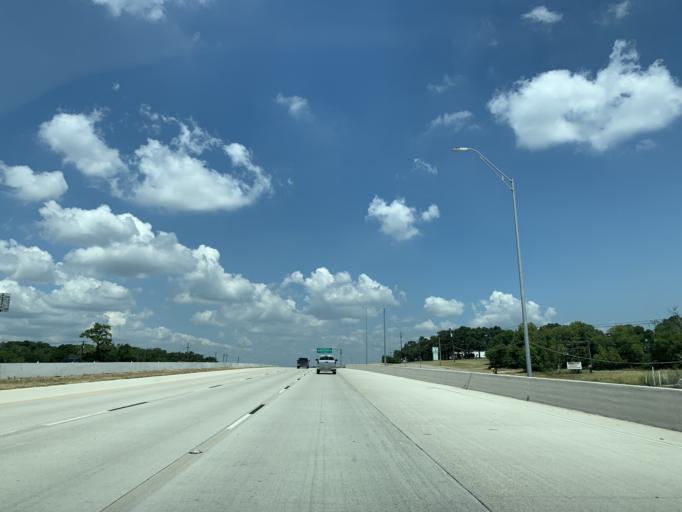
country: US
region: Texas
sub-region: Tarrant County
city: Lakeside
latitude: 32.8446
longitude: -97.4986
